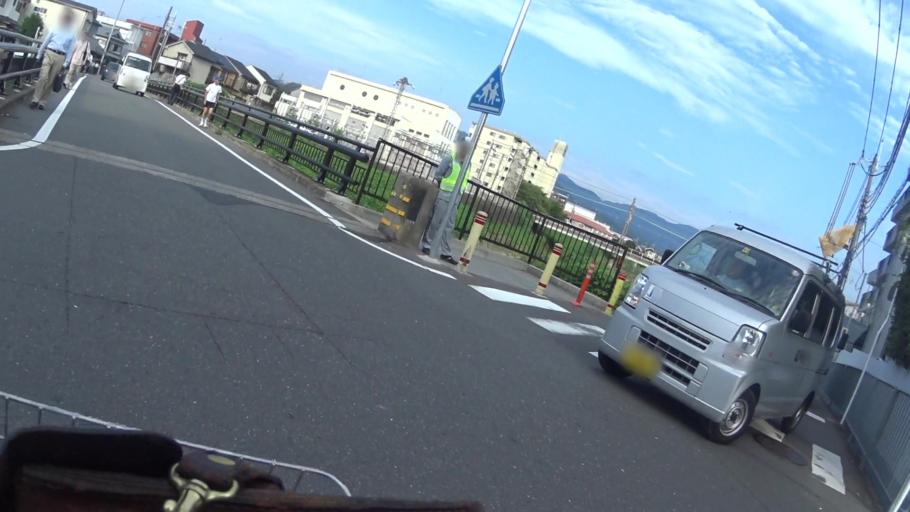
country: JP
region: Kyoto
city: Muko
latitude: 34.9272
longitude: 135.7057
